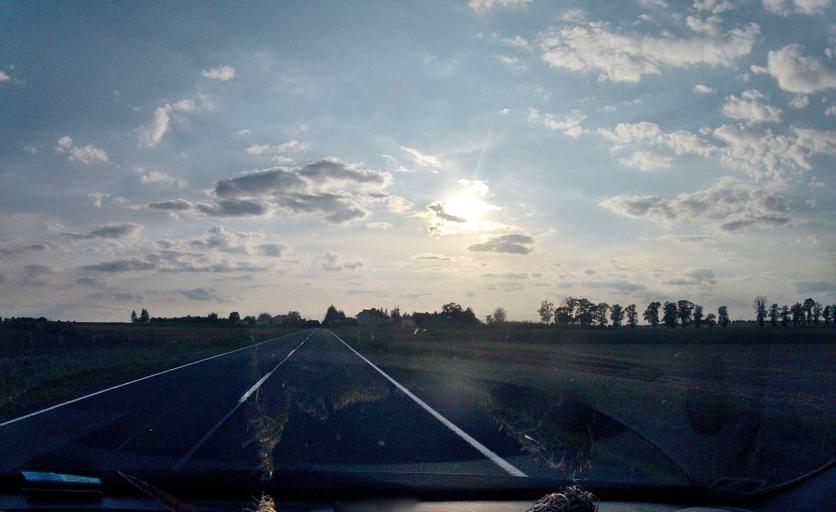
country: PL
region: Opole Voivodeship
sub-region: Powiat oleski
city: Gorzow Slaski
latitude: 51.0034
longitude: 18.3370
